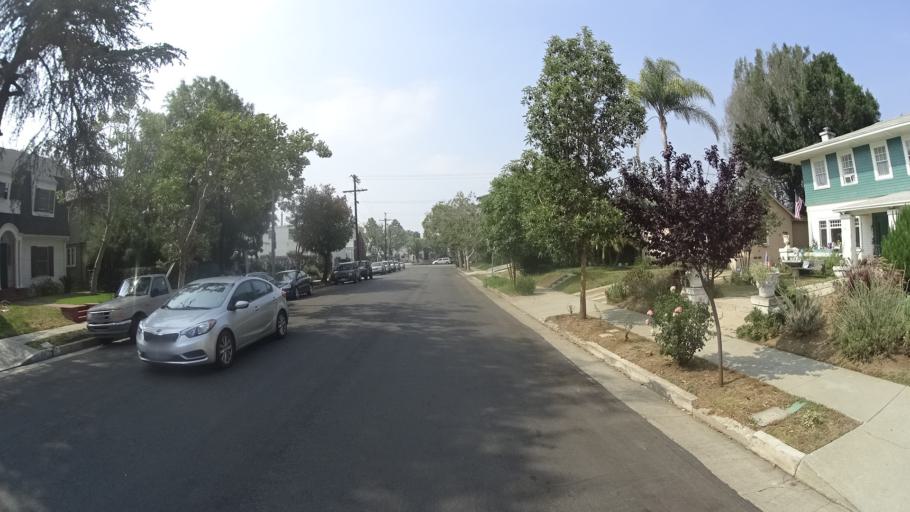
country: US
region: California
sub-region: Los Angeles County
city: View Park-Windsor Hills
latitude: 34.0337
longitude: -118.3249
